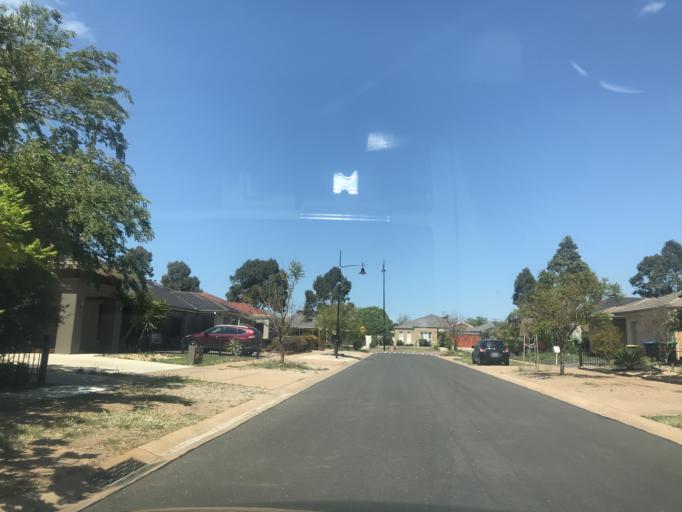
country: AU
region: Victoria
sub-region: Wyndham
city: Hoppers Crossing
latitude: -37.8860
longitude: 144.7270
